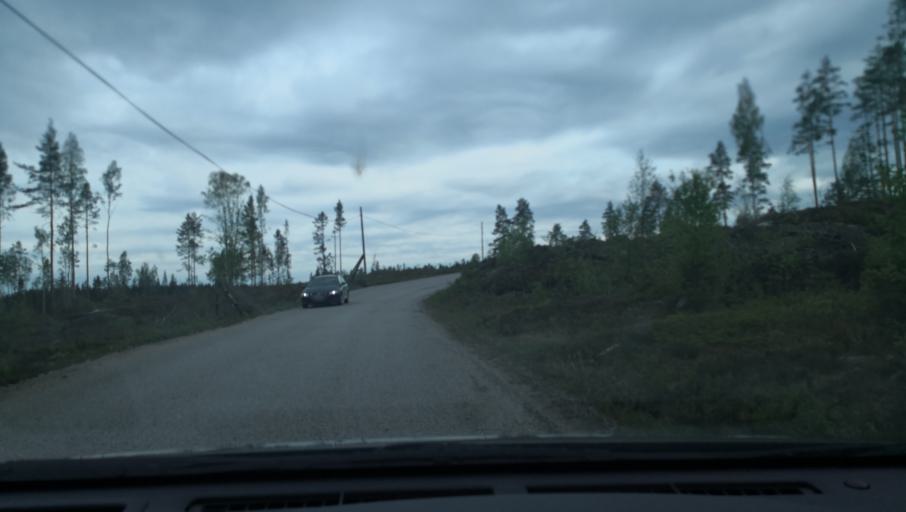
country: SE
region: Vaestmanland
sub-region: Skinnskattebergs Kommun
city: Skinnskatteberg
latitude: 59.8230
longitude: 15.5510
